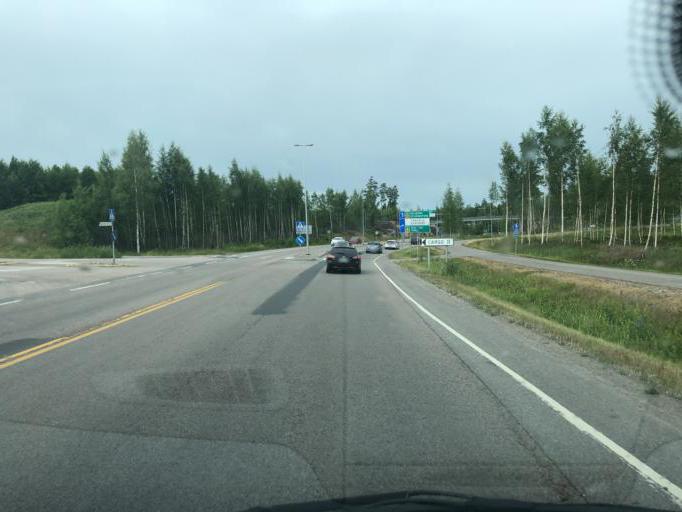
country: FI
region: Uusimaa
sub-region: Helsinki
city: Vantaa
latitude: 60.3061
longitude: 24.9936
